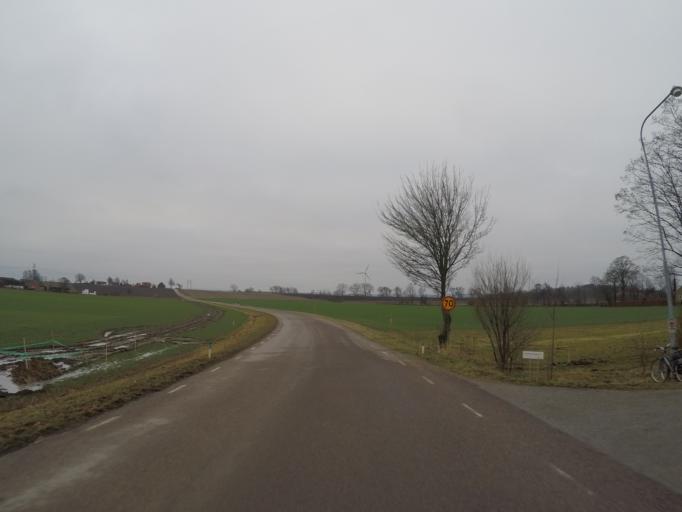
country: SE
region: Skane
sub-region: Hoors Kommun
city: Loberod
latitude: 55.7685
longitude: 13.4456
